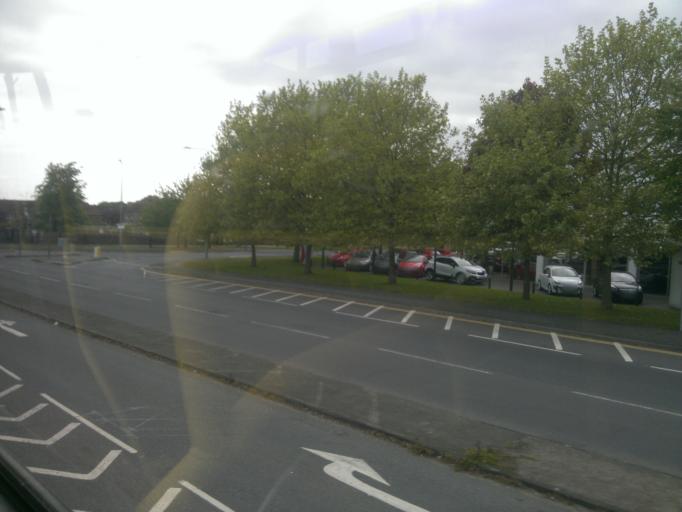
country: GB
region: England
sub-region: Essex
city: Colchester
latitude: 51.9141
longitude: 0.9293
